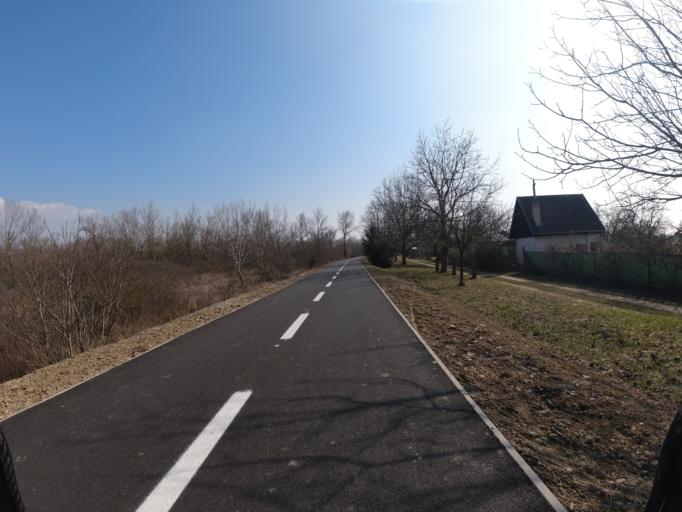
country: SK
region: Trenciansky
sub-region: Okres Nove Mesto nad Vahom
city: Nove Mesto nad Vahom
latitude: 48.7499
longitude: 17.8501
